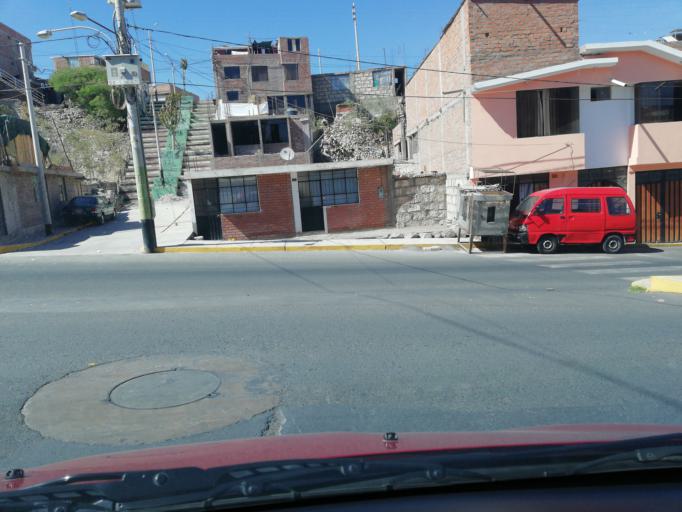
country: PE
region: Arequipa
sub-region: Provincia de Arequipa
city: Arequipa
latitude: -16.3688
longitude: -71.5253
